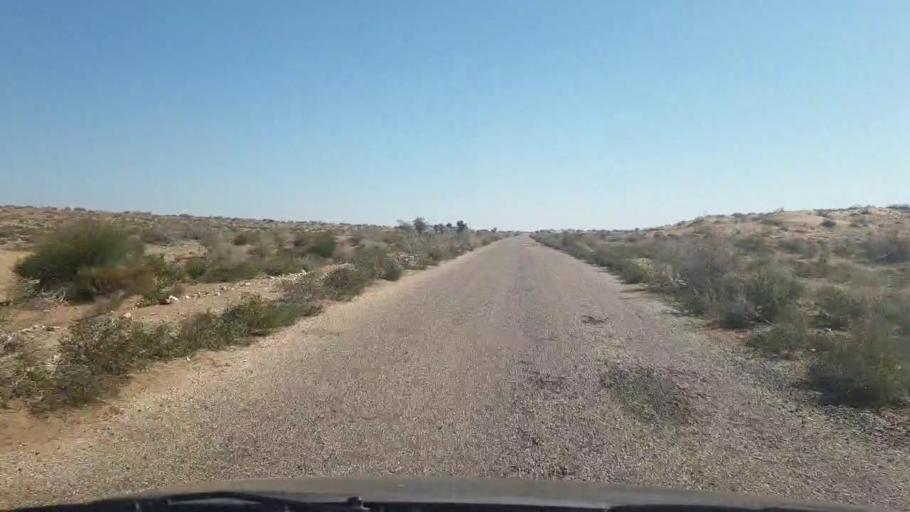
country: PK
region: Sindh
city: Bozdar
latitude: 27.0167
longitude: 68.7794
